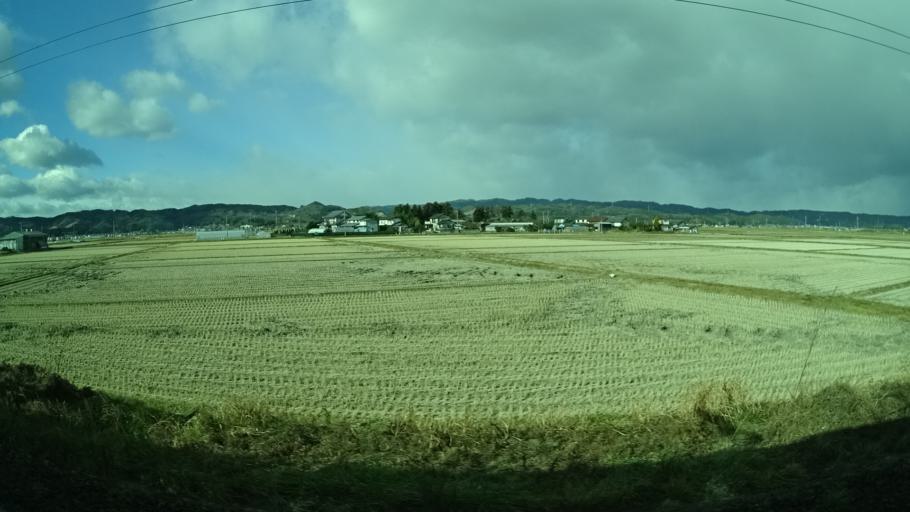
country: JP
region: Miyagi
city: Iwanuma
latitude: 38.1244
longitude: 140.8715
